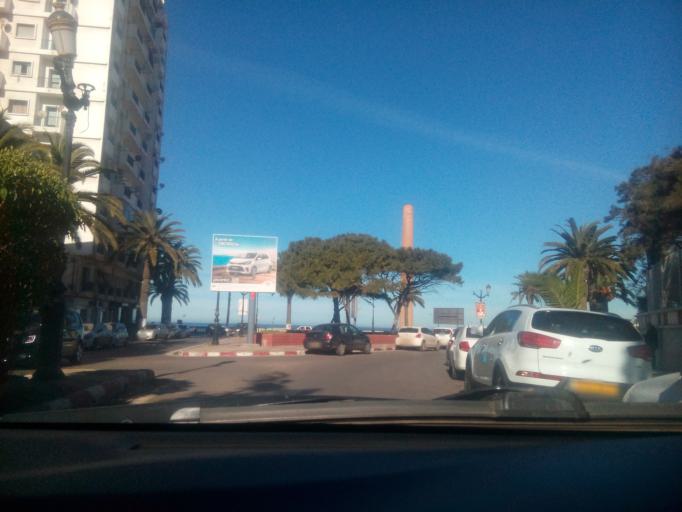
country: DZ
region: Oran
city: Oran
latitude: 35.7062
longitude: -0.6316
